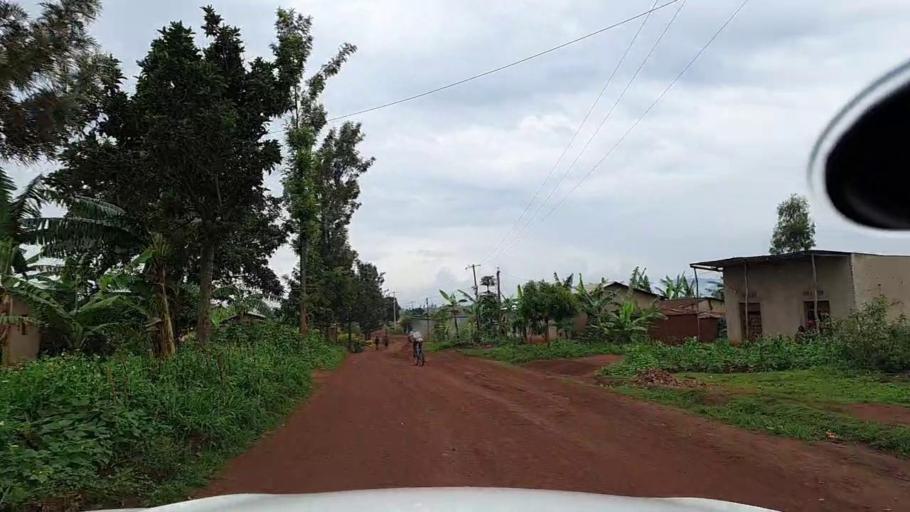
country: RW
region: Kigali
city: Kigali
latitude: -1.9151
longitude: 29.8985
